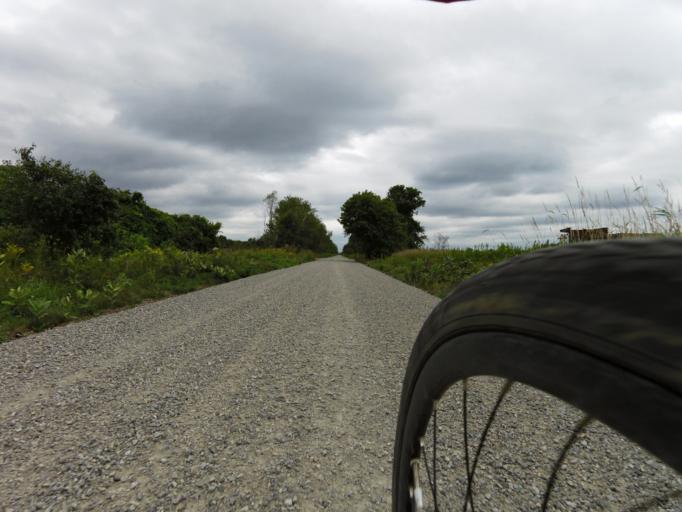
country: CA
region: Ontario
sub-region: Lanark County
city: Smiths Falls
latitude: 44.9314
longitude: -76.0347
